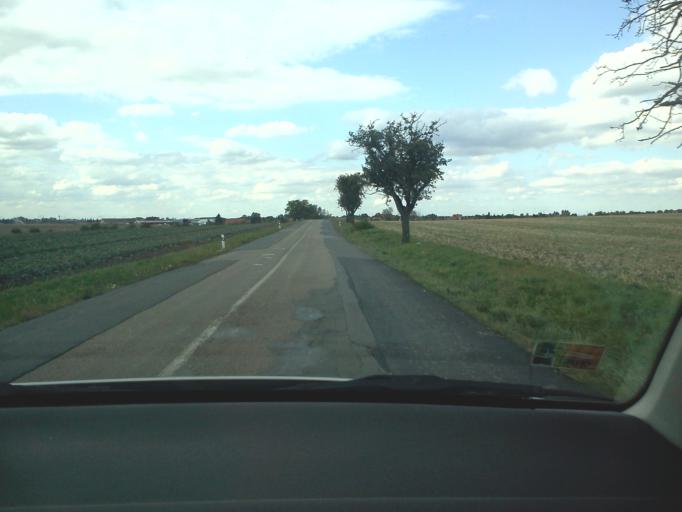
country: CZ
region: Central Bohemia
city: Prerov nad Labem
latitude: 50.1245
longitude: 14.8522
